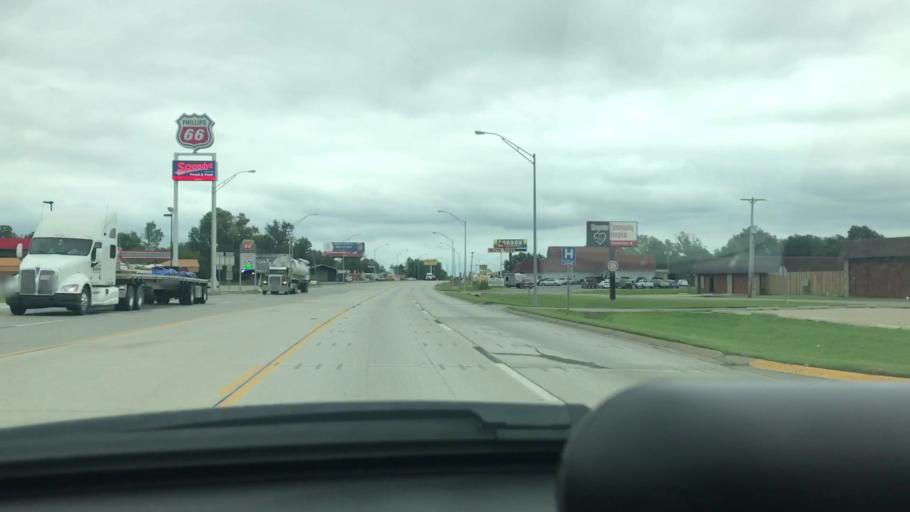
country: US
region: Oklahoma
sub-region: Wagoner County
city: Wagoner
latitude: 35.9610
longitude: -95.3942
